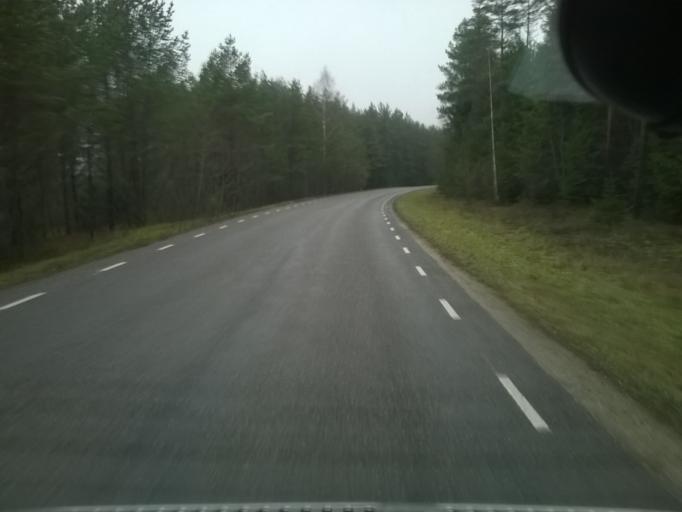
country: EE
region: Raplamaa
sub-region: Kohila vald
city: Kohila
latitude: 59.1940
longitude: 24.6631
